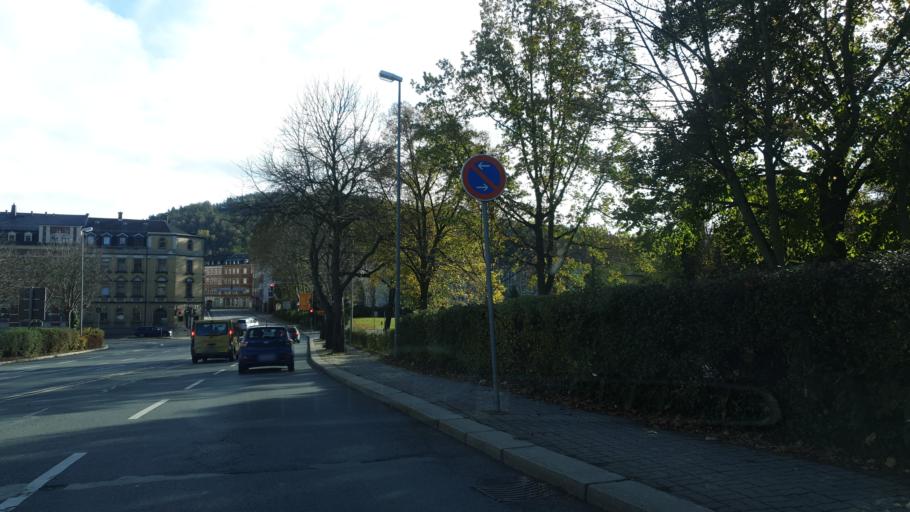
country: DE
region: Saxony
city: Aue
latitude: 50.5889
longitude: 12.6971
